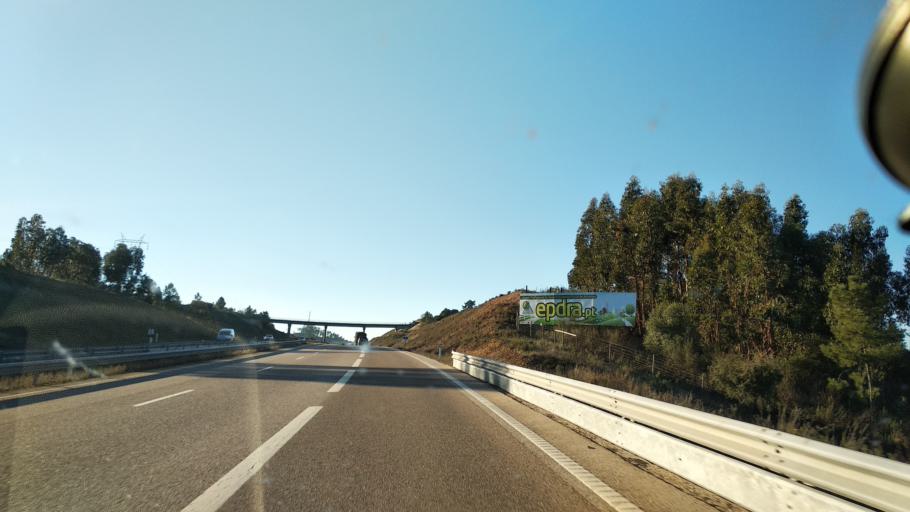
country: PT
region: Santarem
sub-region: Abrantes
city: Alferrarede
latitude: 39.4958
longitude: -8.0767
